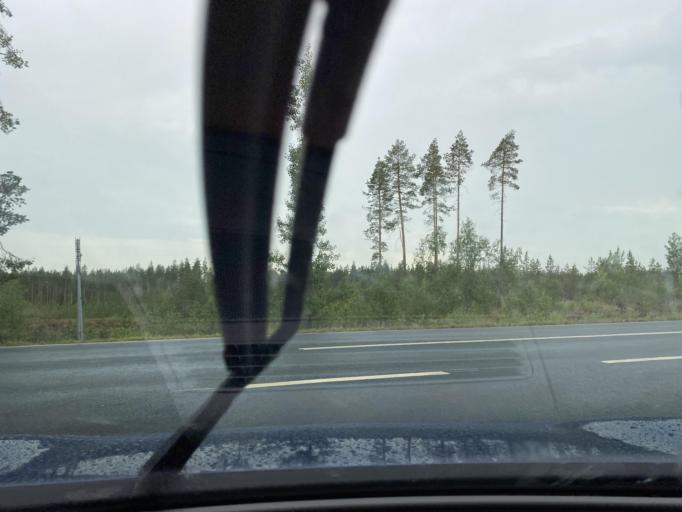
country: FI
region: Central Ostrobothnia
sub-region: Kaustinen
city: Halsua
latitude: 63.4083
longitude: 23.9766
